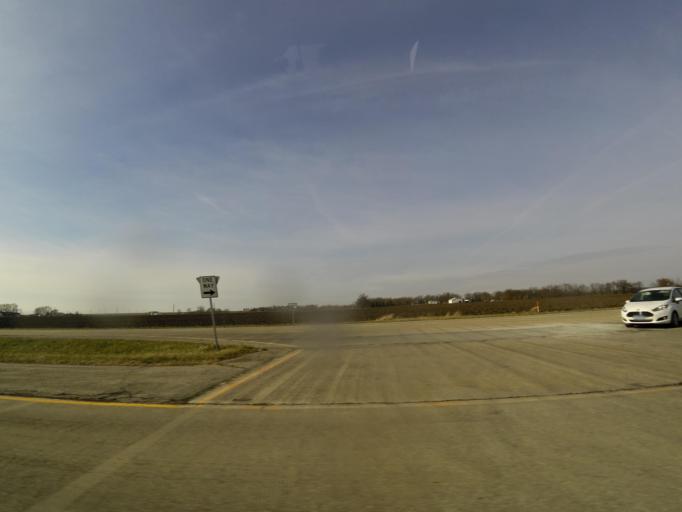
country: US
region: Illinois
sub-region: Macon County
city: Maroa
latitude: 40.0882
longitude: -88.9656
